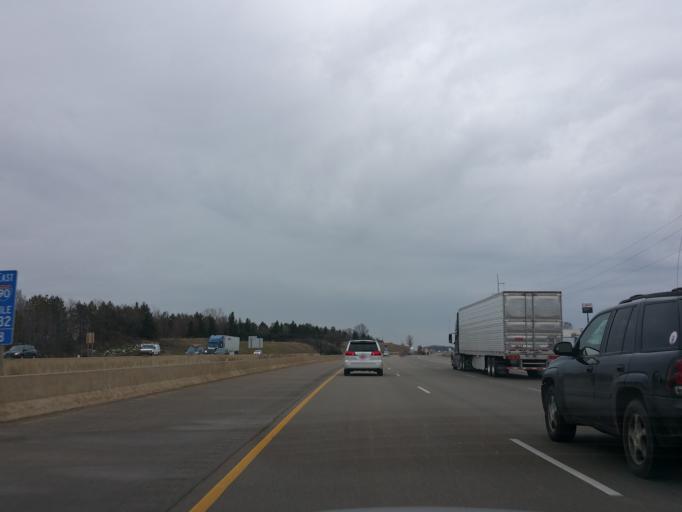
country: US
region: Wisconsin
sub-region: Dane County
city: Windsor
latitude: 43.1769
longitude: -89.3219
